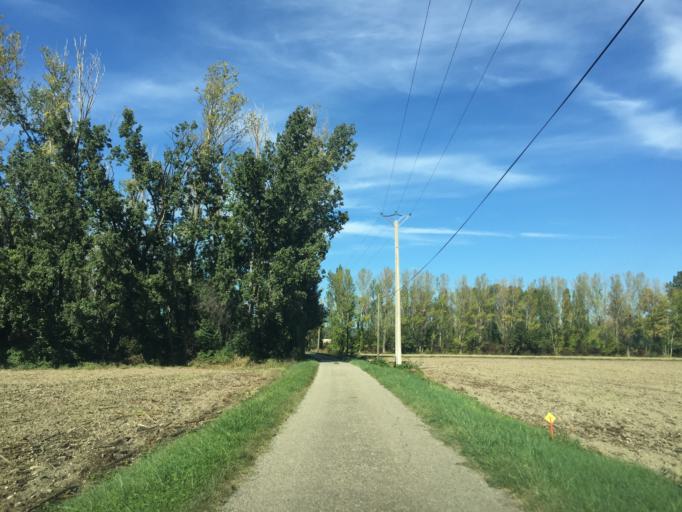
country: FR
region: Provence-Alpes-Cote d'Azur
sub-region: Departement du Vaucluse
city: Piolenc
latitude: 44.1680
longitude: 4.7370
